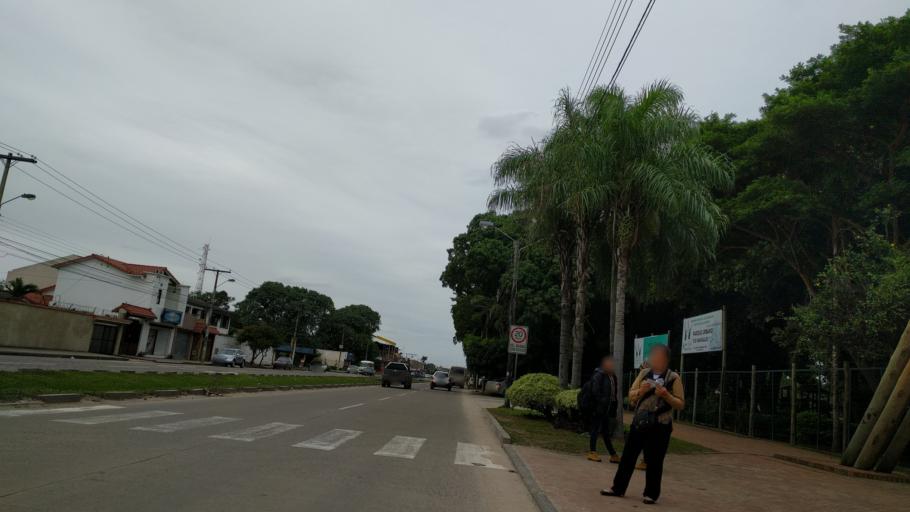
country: BO
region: Santa Cruz
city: Santa Cruz de la Sierra
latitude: -17.7913
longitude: -63.2124
